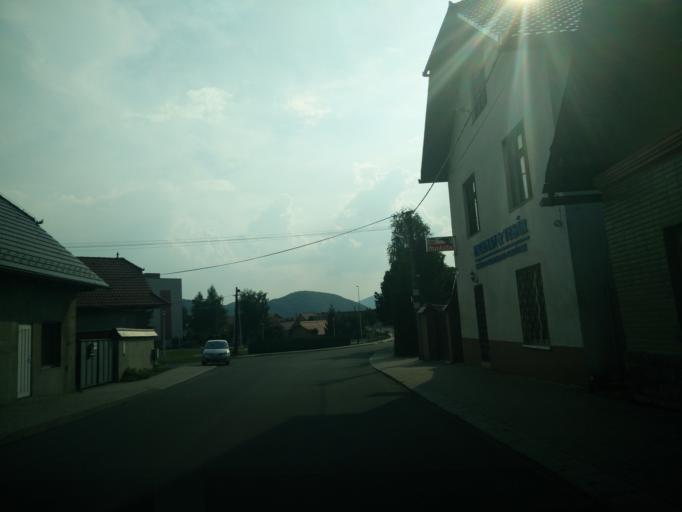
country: SK
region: Banskobystricky
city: Ziar nad Hronom
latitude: 48.5420
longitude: 18.7842
